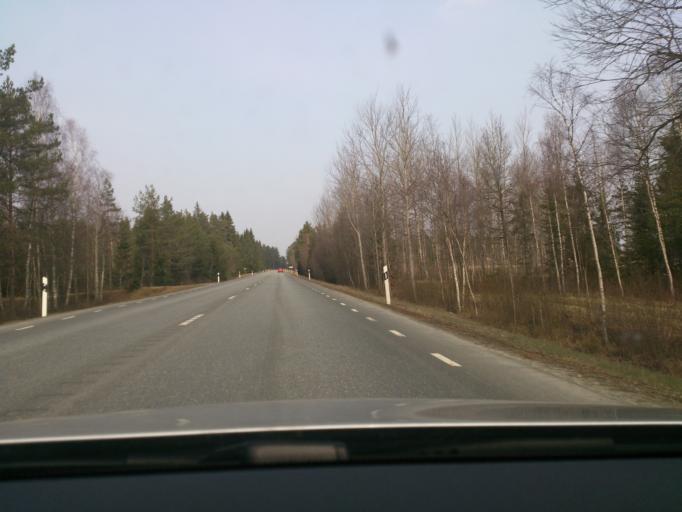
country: SE
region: Kronoberg
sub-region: Alvesta Kommun
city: Moheda
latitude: 56.9865
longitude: 14.5650
